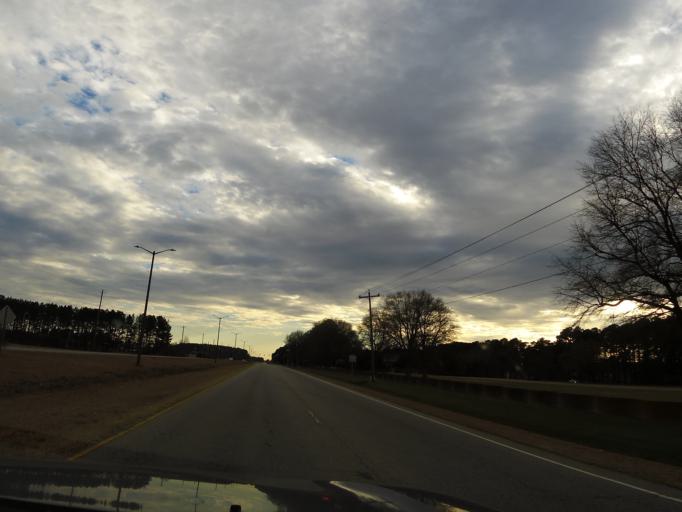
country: US
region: North Carolina
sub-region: Nash County
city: Rocky Mount
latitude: 36.0208
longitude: -77.7698
